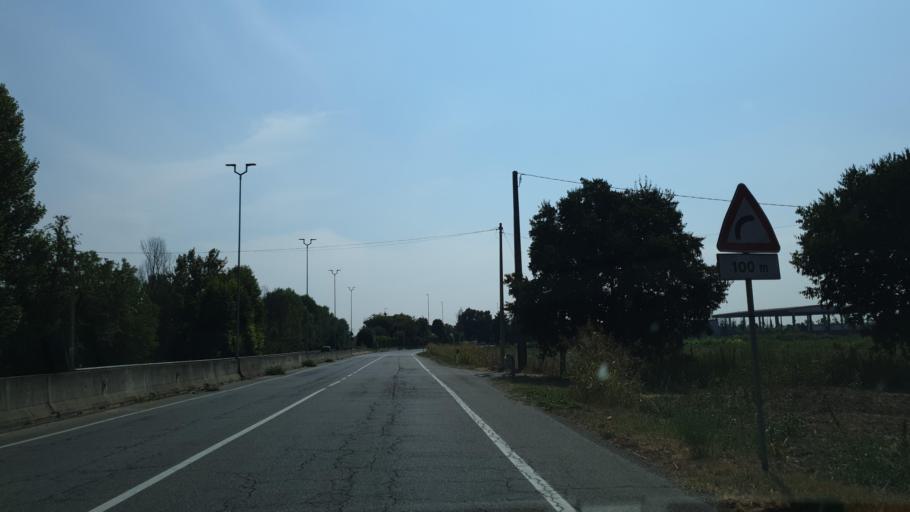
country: IT
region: Lombardy
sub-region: Provincia di Brescia
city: Leno
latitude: 45.3531
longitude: 10.2256
